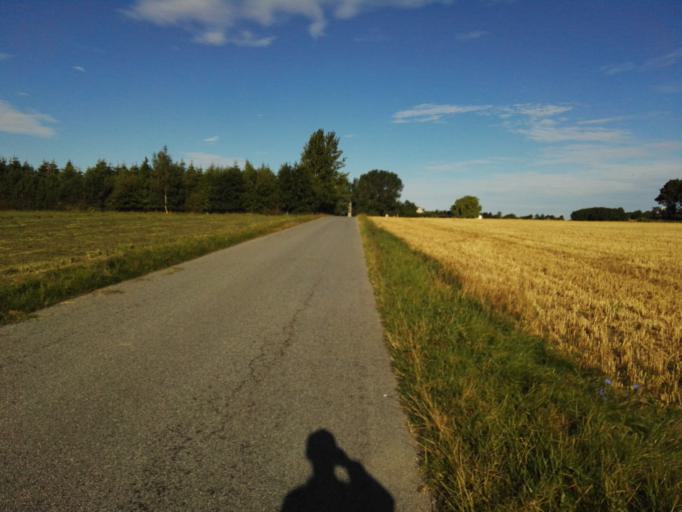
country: DK
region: Capital Region
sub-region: Halsnaes Kommune
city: Hundested
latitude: 55.9586
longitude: 11.7681
